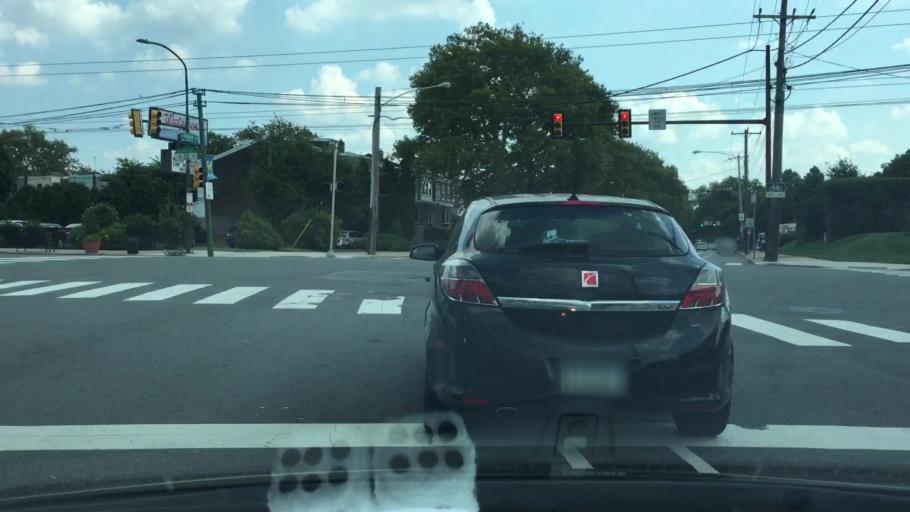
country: US
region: New Jersey
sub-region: Burlington County
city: Palmyra
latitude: 40.0338
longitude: -75.0470
